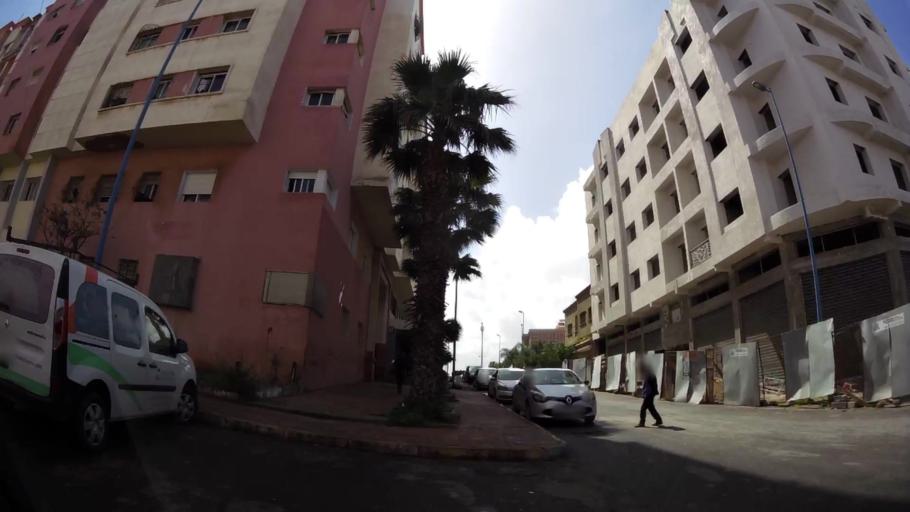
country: MA
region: Grand Casablanca
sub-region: Mediouna
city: Tit Mellil
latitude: 33.6146
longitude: -7.5273
